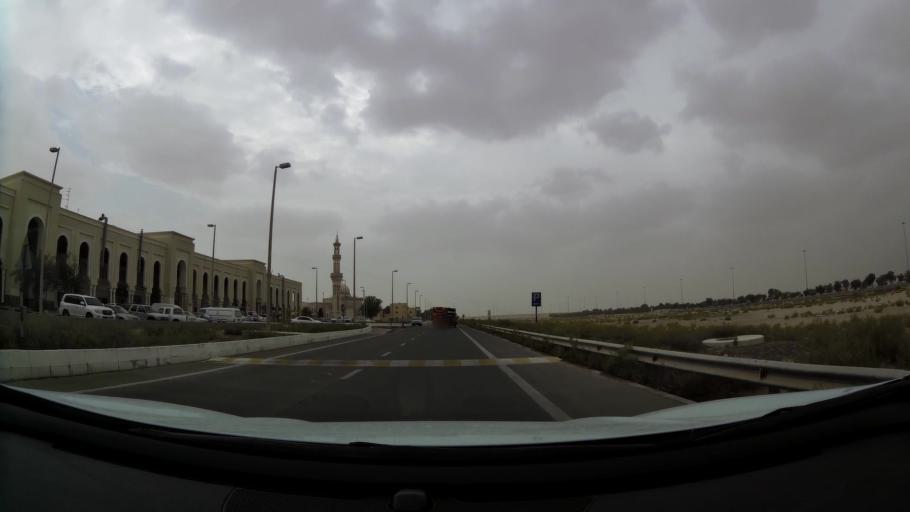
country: AE
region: Abu Dhabi
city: Abu Dhabi
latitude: 24.3760
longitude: 54.6600
